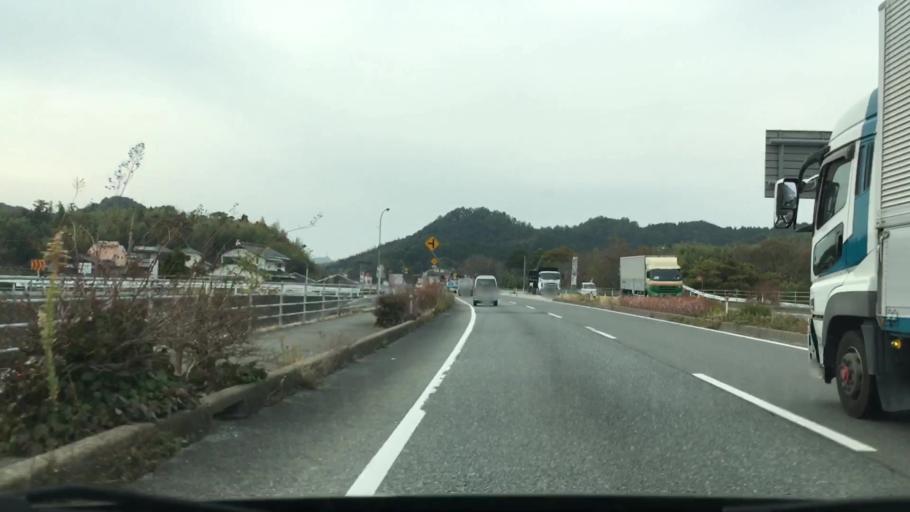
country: JP
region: Yamaguchi
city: Hofu
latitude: 34.0637
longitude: 131.4878
